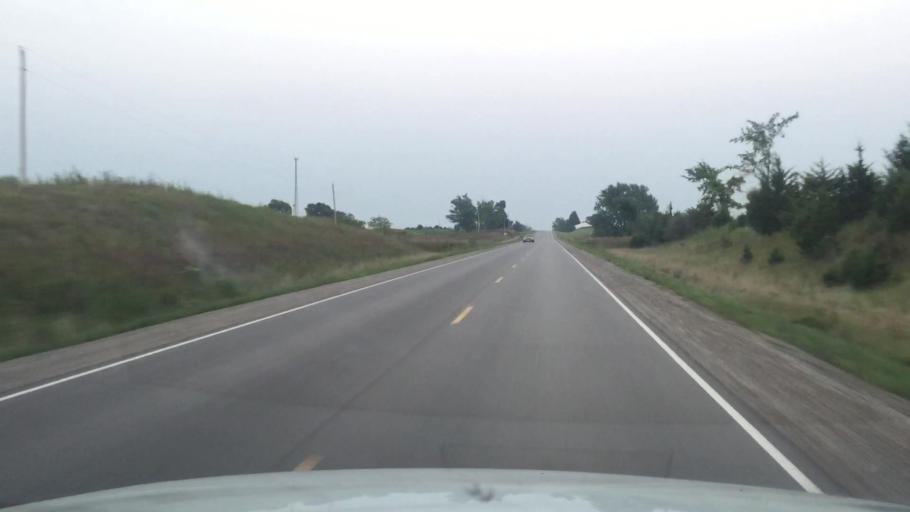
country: US
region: Iowa
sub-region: Marion County
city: Melcher-Dallas
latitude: 41.1895
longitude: -93.4123
